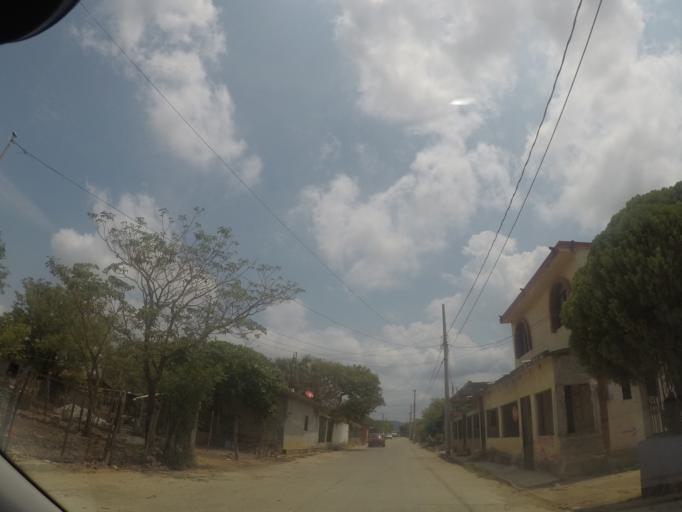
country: MX
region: Oaxaca
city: El Espinal
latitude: 16.5540
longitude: -94.9453
